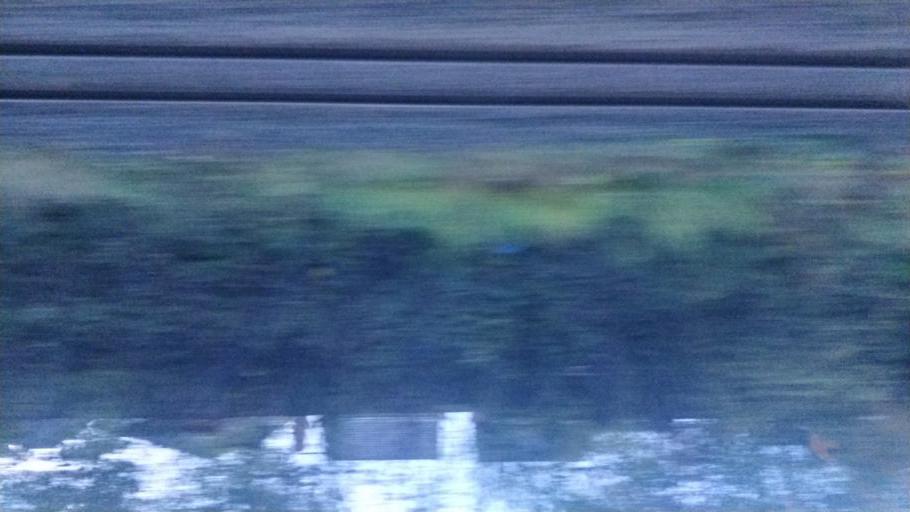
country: GB
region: England
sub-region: Borough of Bolton
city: Westhoughton
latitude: 53.5398
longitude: -2.5170
